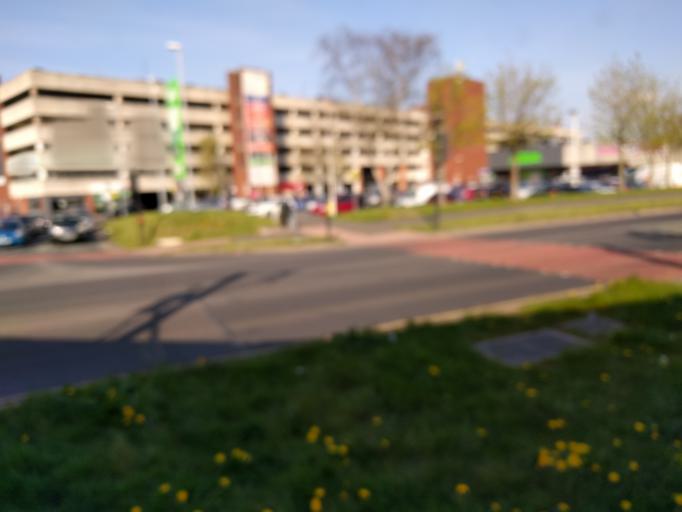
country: GB
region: England
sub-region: Manchester
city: Ringway
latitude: 53.3784
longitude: -2.2645
